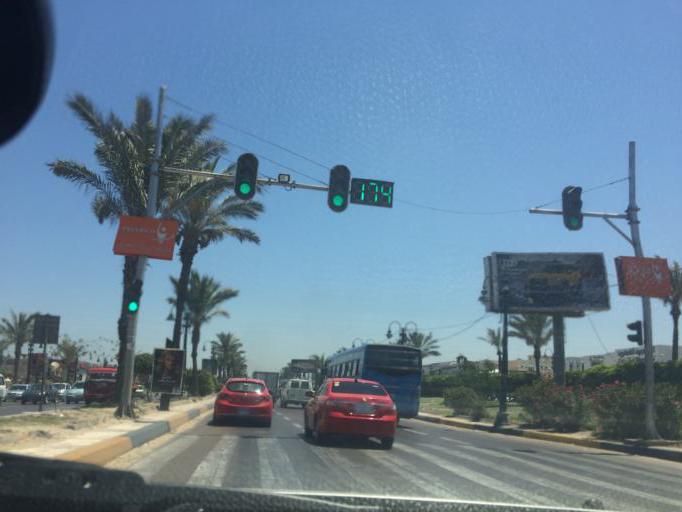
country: EG
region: Alexandria
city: Alexandria
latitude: 31.1742
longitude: 29.9319
